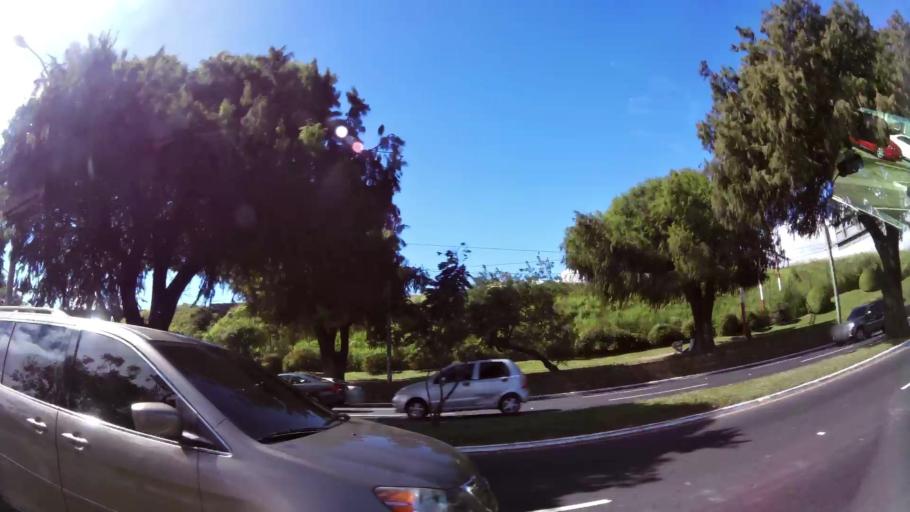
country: GT
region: Guatemala
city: Santa Catarina Pinula
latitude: 14.5970
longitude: -90.5227
